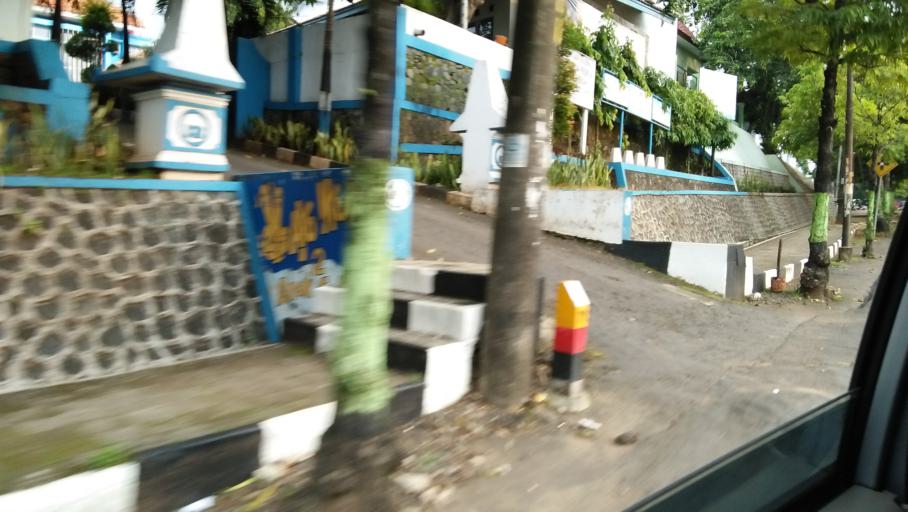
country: ID
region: Central Java
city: Mlonggo
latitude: -6.5887
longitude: 110.6762
